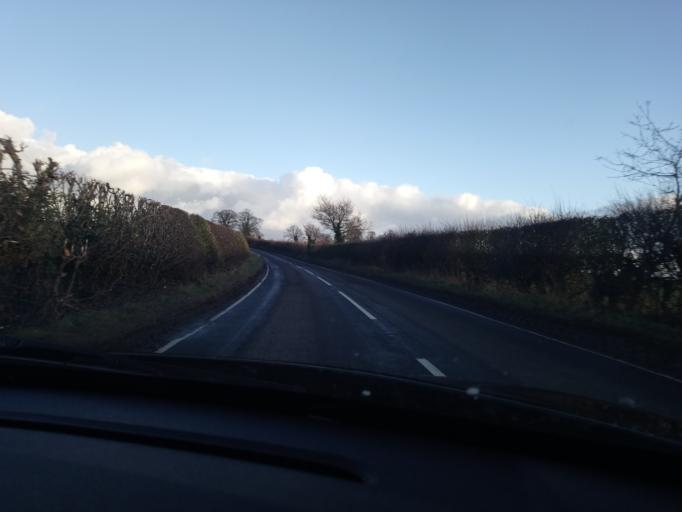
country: GB
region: England
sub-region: Shropshire
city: Wem
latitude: 52.8612
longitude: -2.7536
